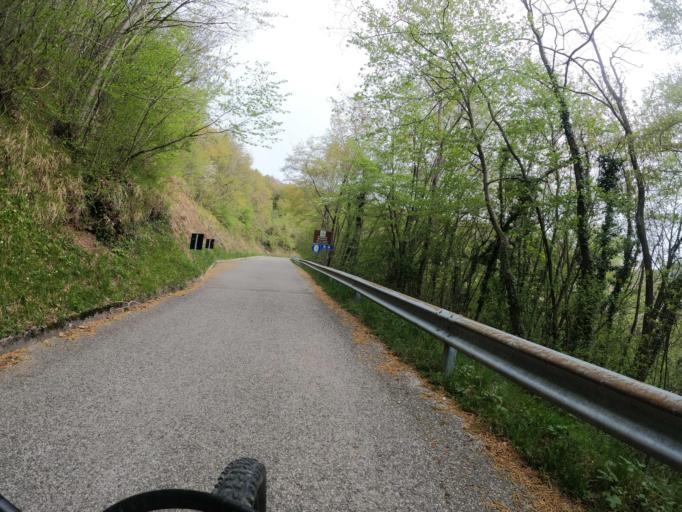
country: IT
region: Friuli Venezia Giulia
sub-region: Provincia di Udine
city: Stregna
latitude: 46.1384
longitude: 13.5767
